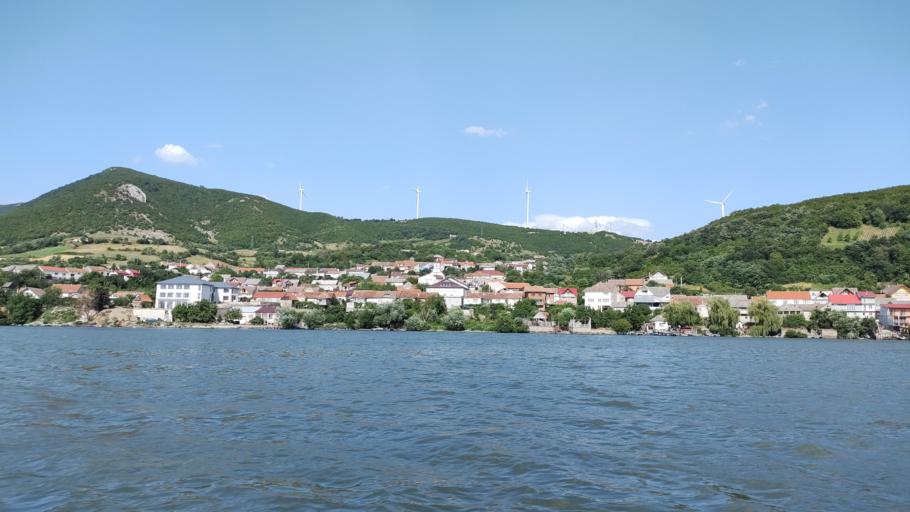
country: RO
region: Caras-Severin
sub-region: Comuna Pescari
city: Coronini
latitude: 44.6777
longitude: 21.6759
